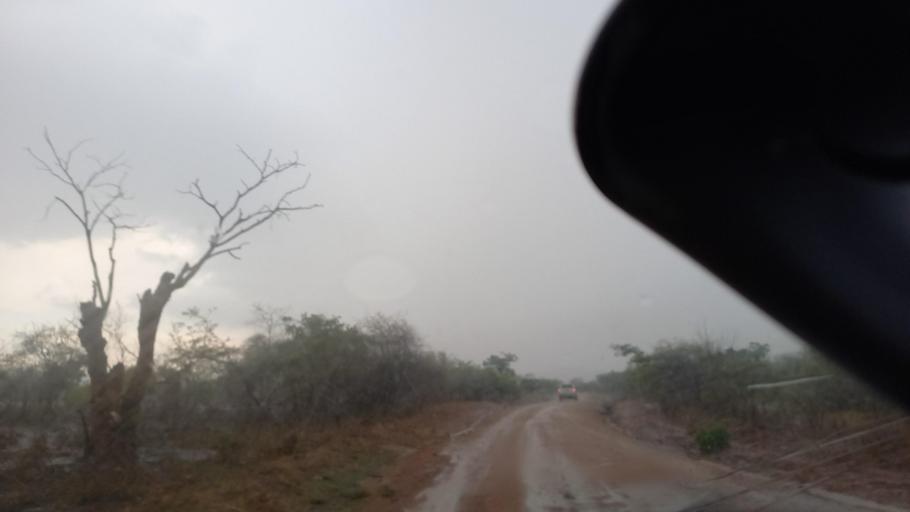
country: ZM
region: Lusaka
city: Kafue
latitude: -15.9367
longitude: 28.2114
